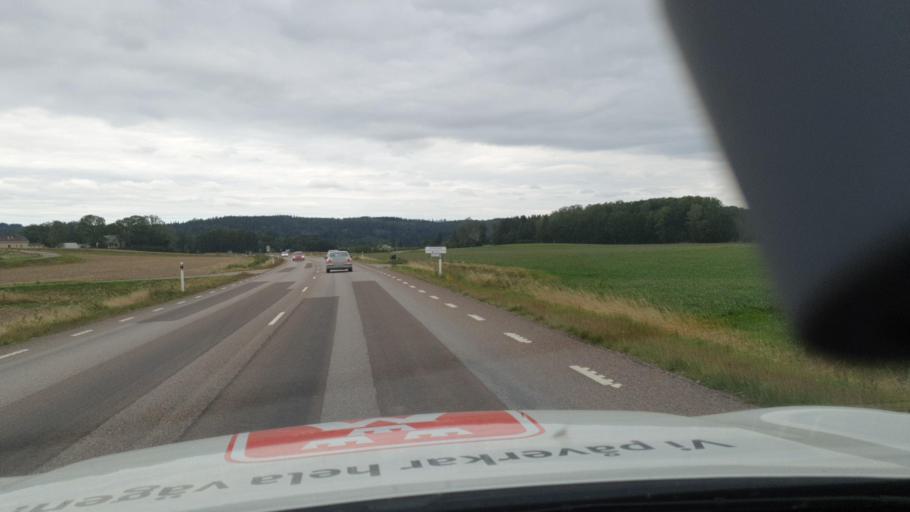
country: SE
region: Vaestra Goetaland
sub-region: Melleruds Kommun
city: Mellerud
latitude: 58.7248
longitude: 12.3913
